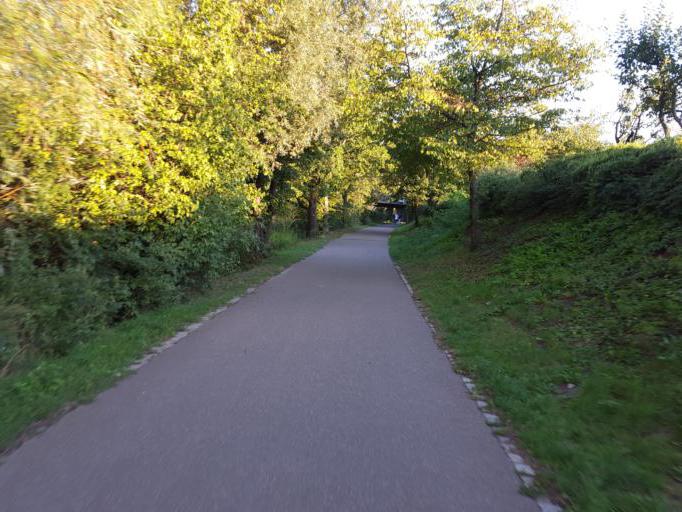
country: DE
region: Baden-Wuerttemberg
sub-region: Karlsruhe Region
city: Karlsruhe
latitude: 49.0011
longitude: 8.3703
